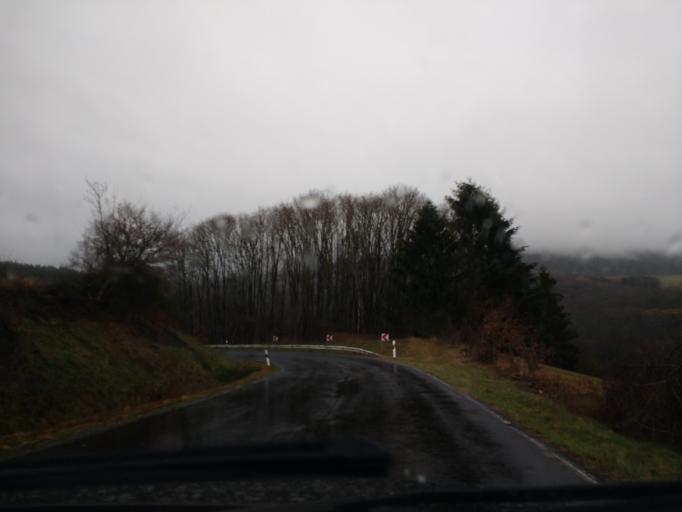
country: DE
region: Rheinland-Pfalz
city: Hilscheid
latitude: 49.7278
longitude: 7.0051
